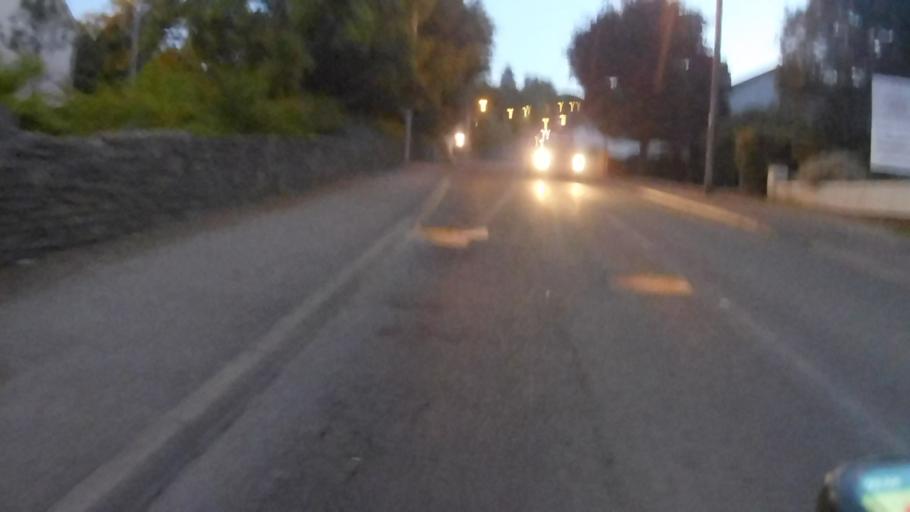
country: IE
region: Munster
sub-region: County Cork
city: Passage West
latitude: 51.9275
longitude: -8.3968
